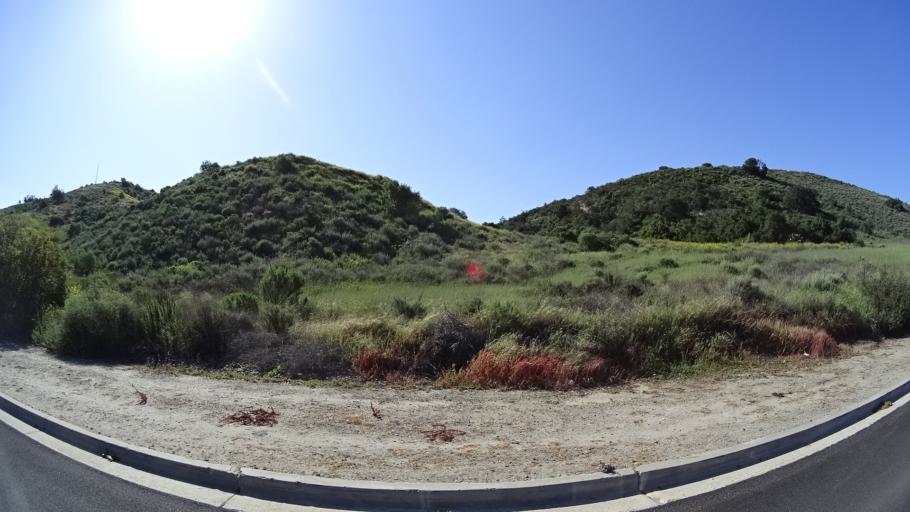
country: US
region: California
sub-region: Ventura County
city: Simi Valley
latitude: 34.2439
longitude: -118.8358
